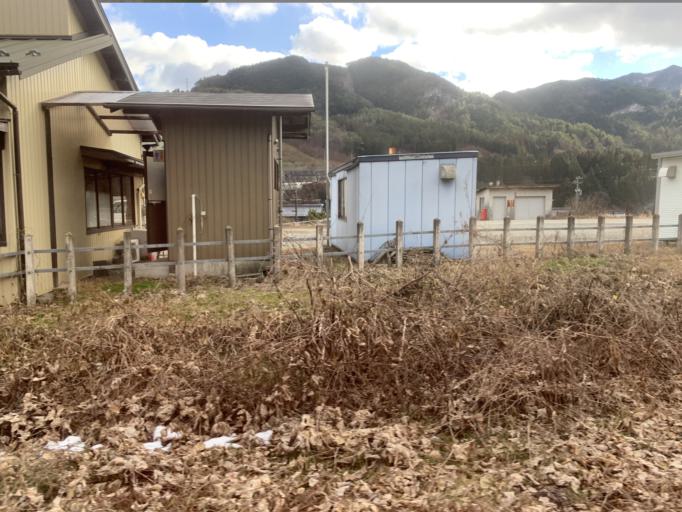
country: JP
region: Gifu
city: Takayama
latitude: 35.9492
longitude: 137.2554
